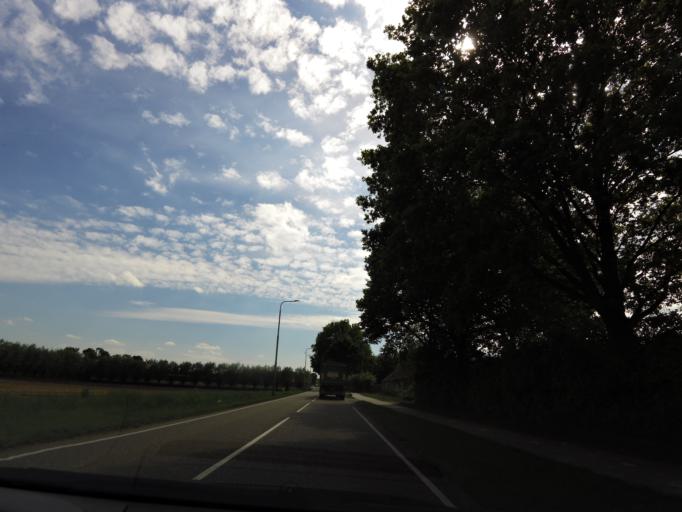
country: NL
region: Limburg
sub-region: Gemeente Leudal
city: Haelen
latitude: 51.3039
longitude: 5.9697
